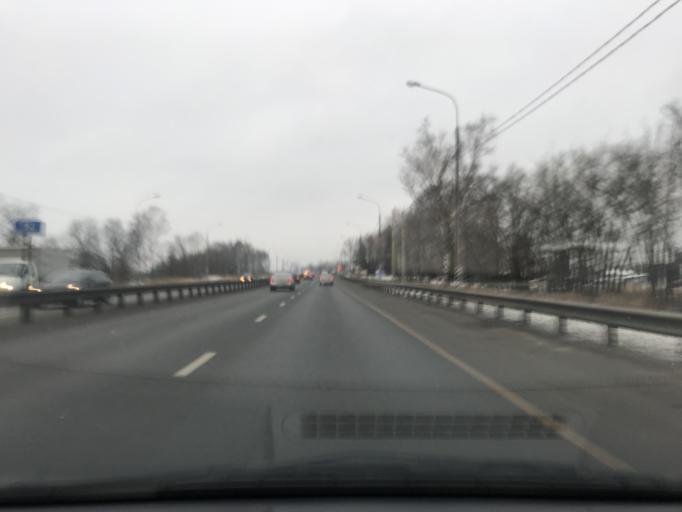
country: RU
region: Moskovskaya
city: Elektrostal'
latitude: 55.8269
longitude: 38.4165
